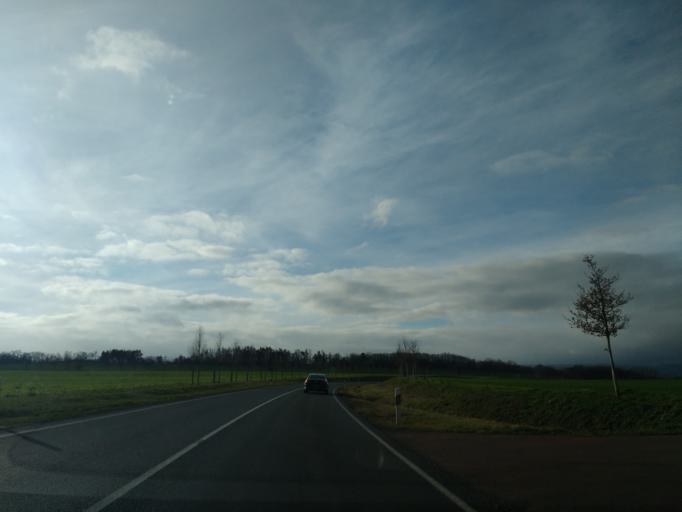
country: DE
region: Saxony-Anhalt
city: Quedlinburg
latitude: 51.7810
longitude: 11.1795
